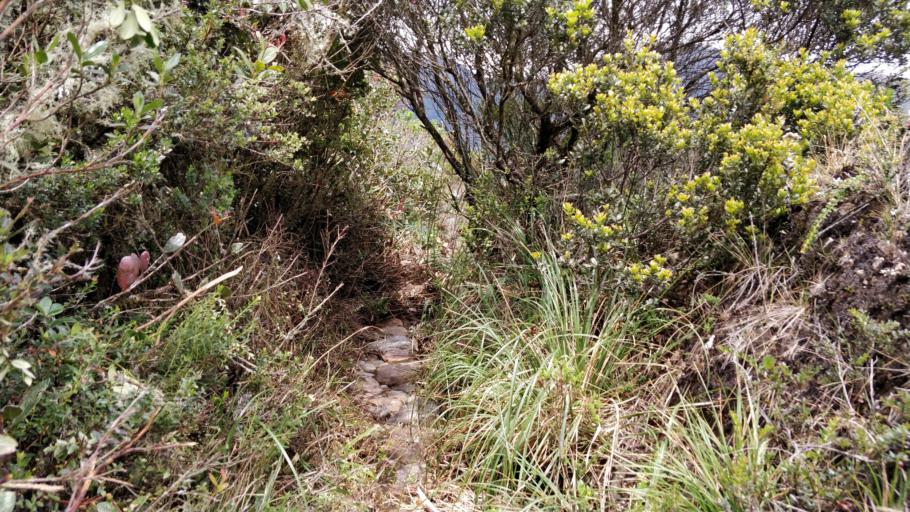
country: CO
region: Bogota D.C.
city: Bogota
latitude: 4.5299
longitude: -74.0472
